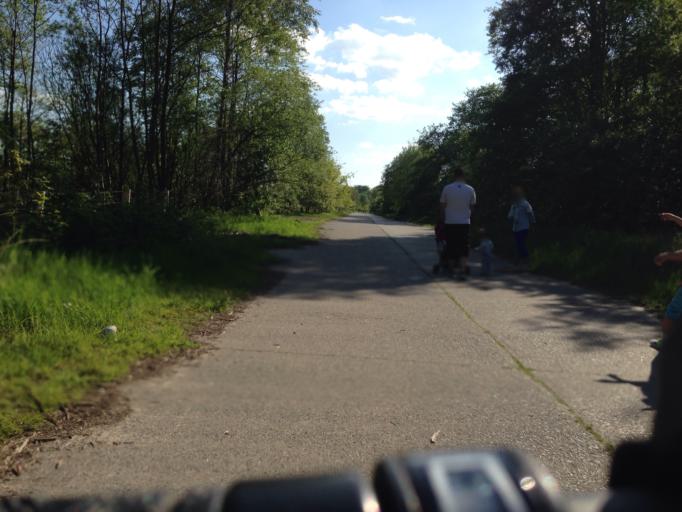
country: DE
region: Schleswig-Holstein
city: Stapelfeld
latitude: 53.6155
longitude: 10.1928
